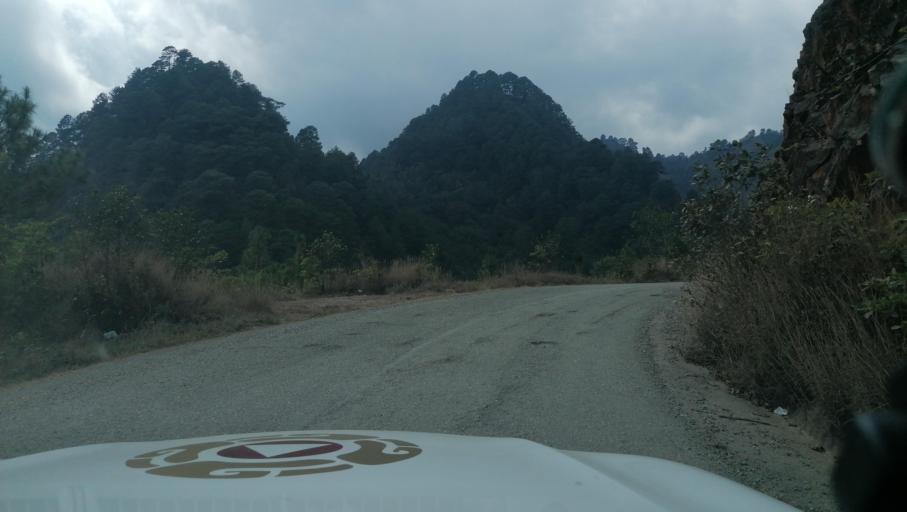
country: GT
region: San Marcos
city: Tacana
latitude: 15.2138
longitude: -92.2004
